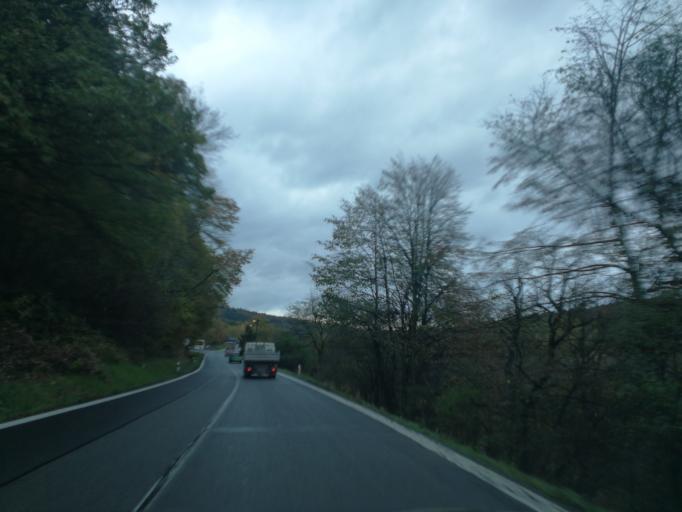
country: CZ
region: Zlin
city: Valasske Mezirici
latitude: 49.4990
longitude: 17.9928
